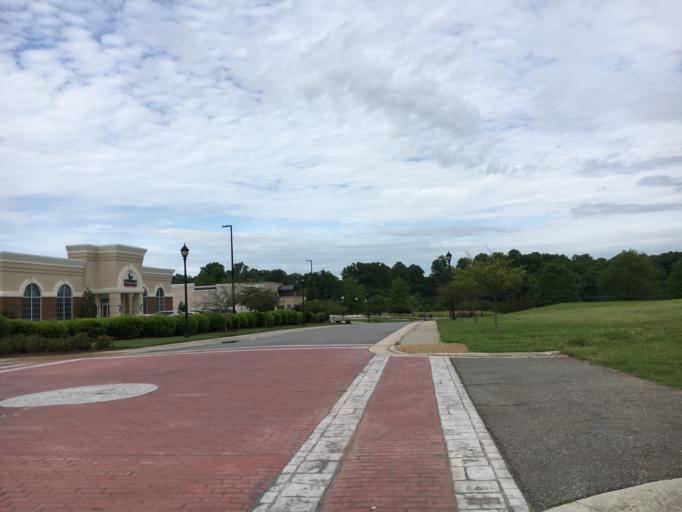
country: US
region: Virginia
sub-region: Bedford County
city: Forest
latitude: 37.3672
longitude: -79.2607
